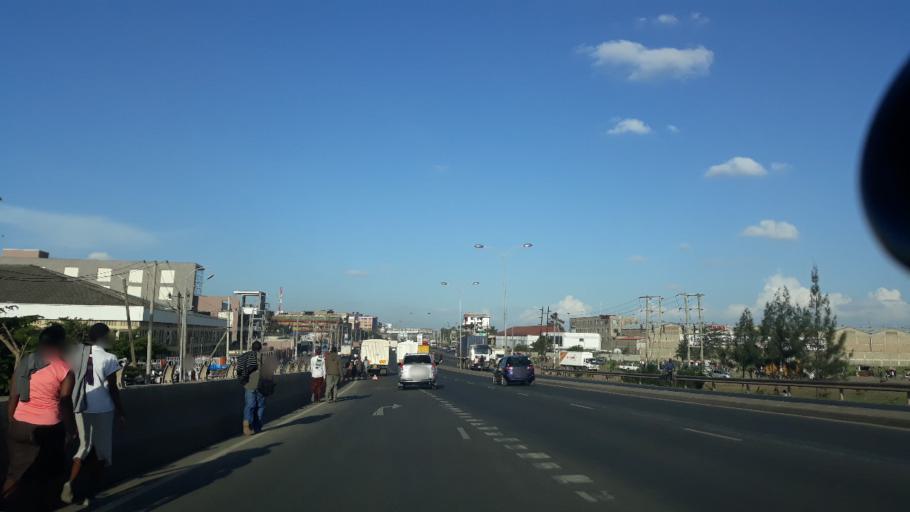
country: KE
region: Nairobi Area
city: Pumwani
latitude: -1.3307
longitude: 36.8894
